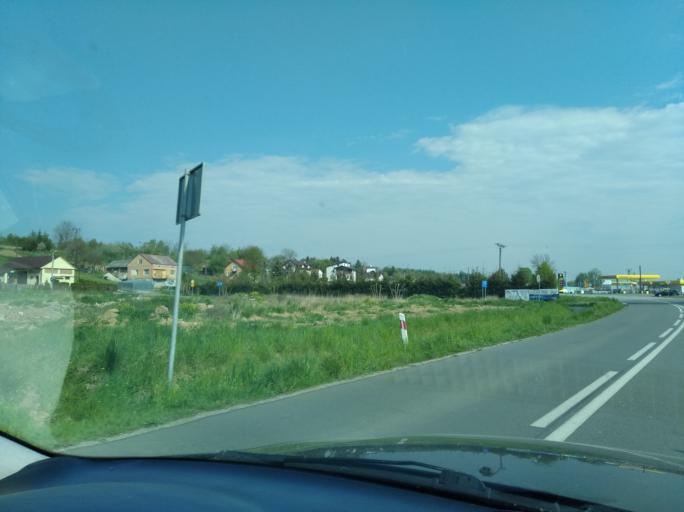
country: PL
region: Subcarpathian Voivodeship
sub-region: Powiat rzeszowski
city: Dynow
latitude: 49.8007
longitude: 22.2410
